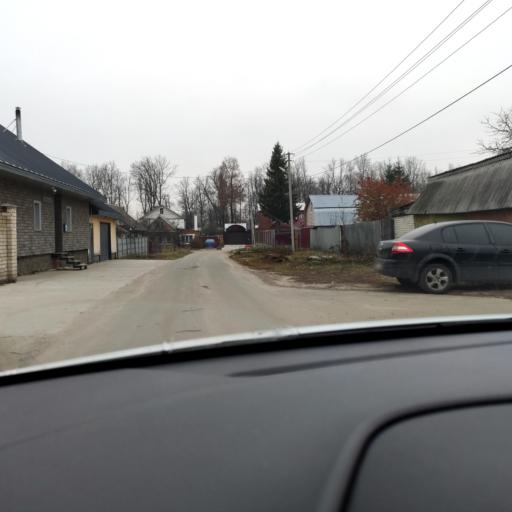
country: RU
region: Tatarstan
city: Vysokaya Gora
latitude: 55.8490
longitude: 49.2154
